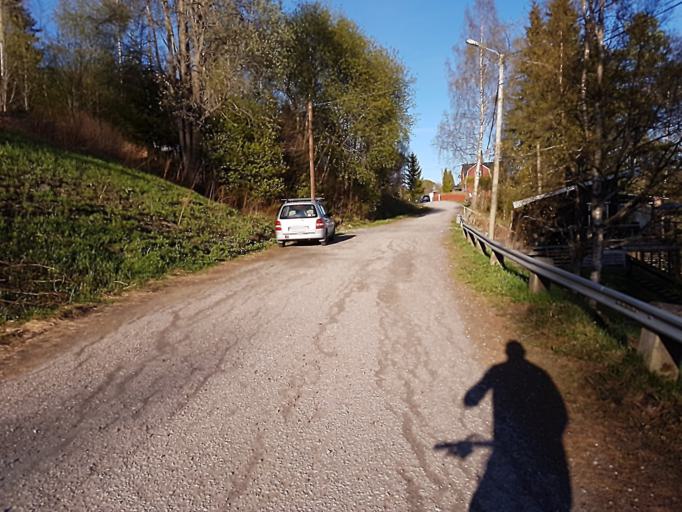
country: SE
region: Vaesternorrland
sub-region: Sundsvalls Kommun
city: Vi
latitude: 62.3252
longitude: 17.2121
